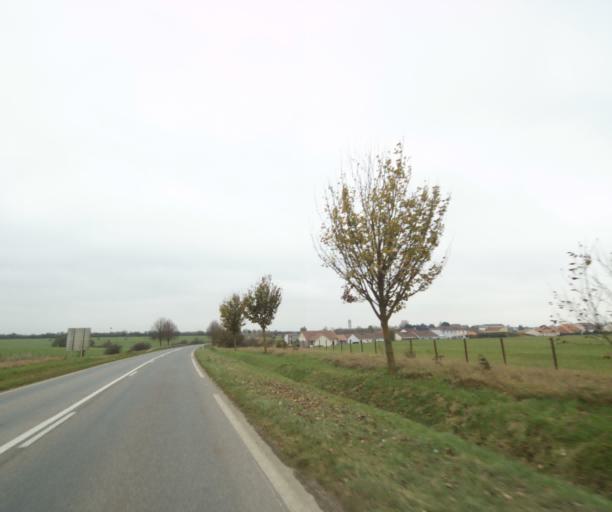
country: FR
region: Lorraine
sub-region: Departement de Meurthe-et-Moselle
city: Briey
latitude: 49.2545
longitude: 5.9496
